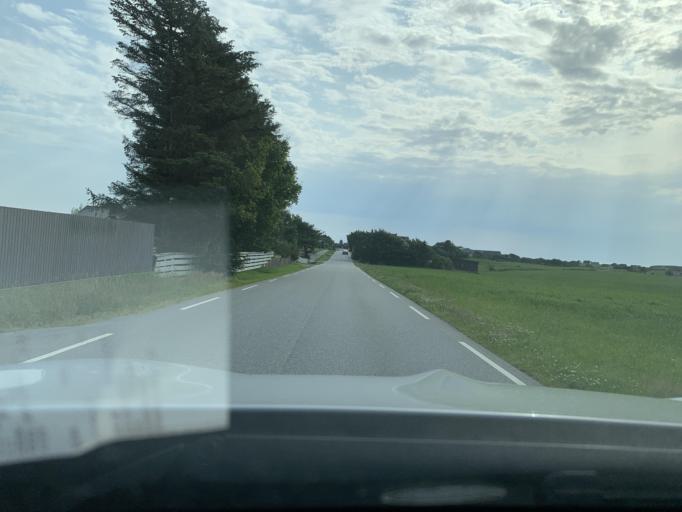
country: NO
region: Rogaland
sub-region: Time
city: Bryne
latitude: 58.7228
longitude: 5.5766
